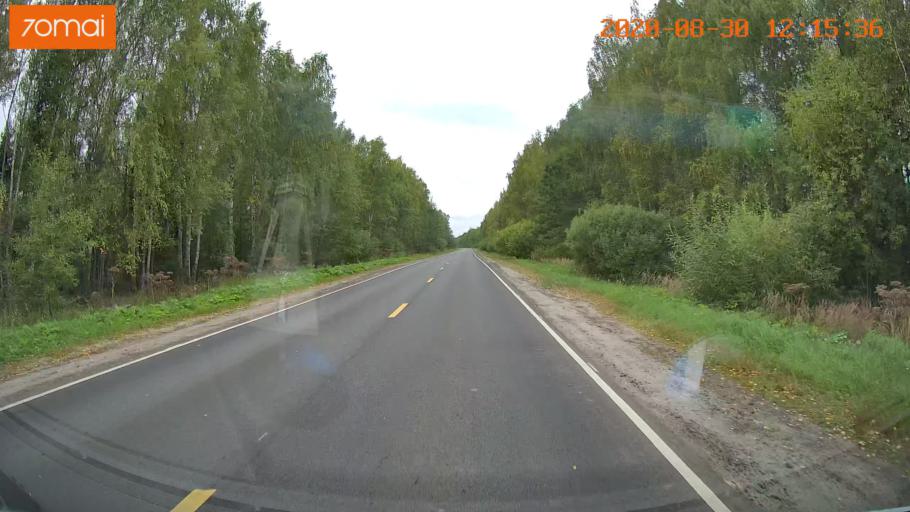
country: RU
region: Ivanovo
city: Yur'yevets
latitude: 57.3178
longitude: 43.0255
